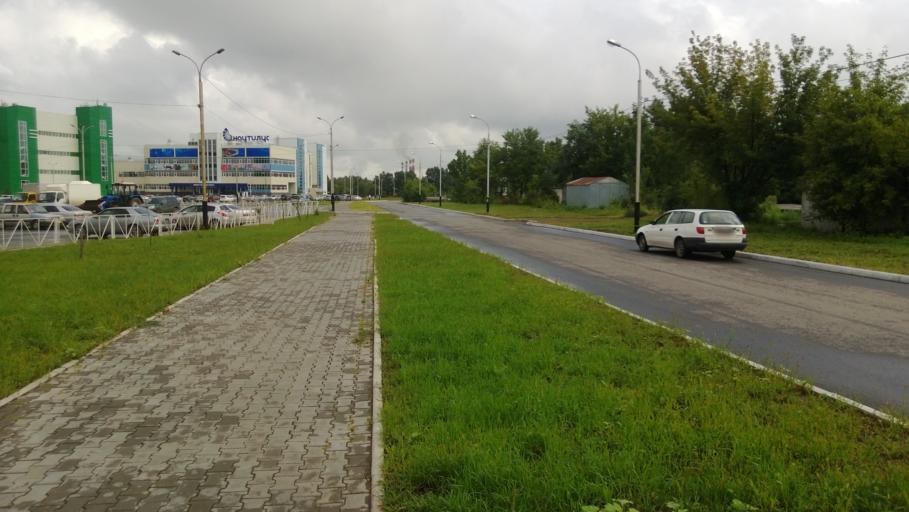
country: RU
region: Khabarovsk Krai
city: Khabarovsk Vtoroy
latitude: 48.3941
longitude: 135.1074
